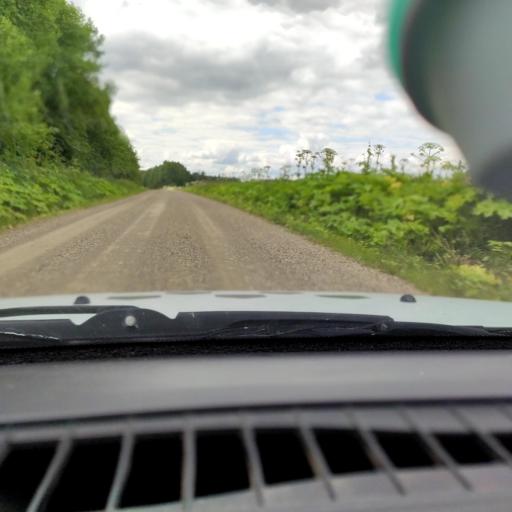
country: RU
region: Perm
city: Suksun
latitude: 57.2094
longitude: 57.6511
